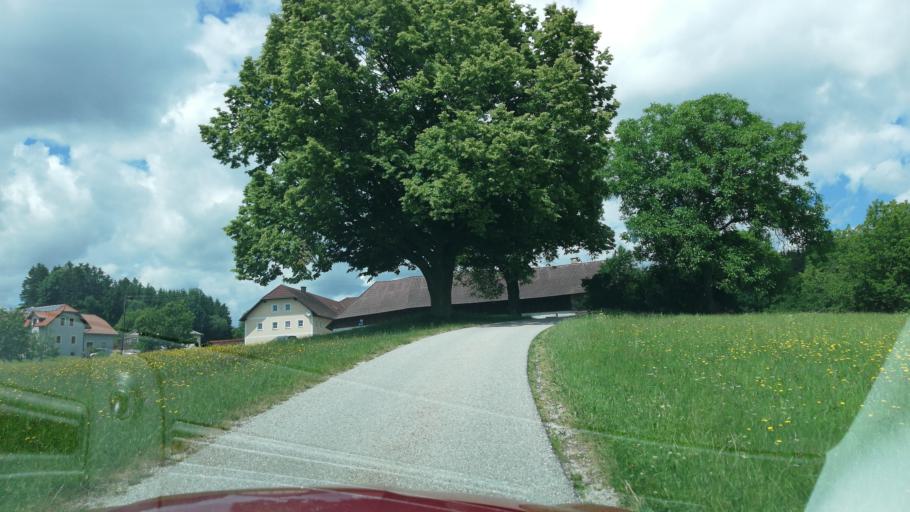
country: AT
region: Upper Austria
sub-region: Politischer Bezirk Urfahr-Umgebung
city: Haibach im Muhlkreis
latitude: 48.4268
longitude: 14.3604
